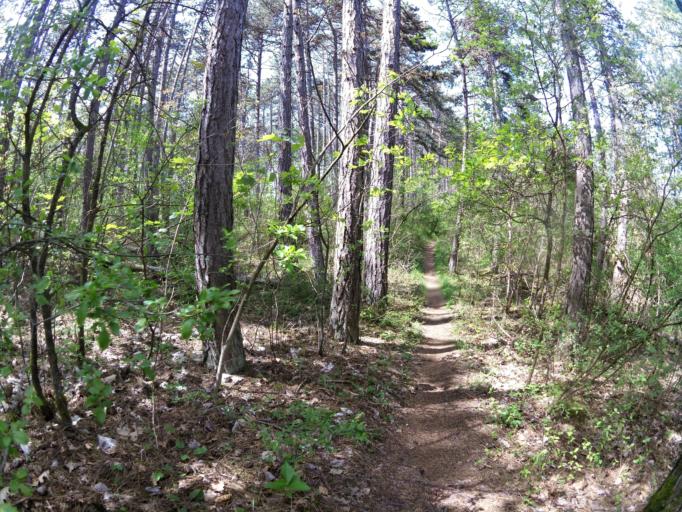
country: DE
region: Bavaria
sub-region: Regierungsbezirk Unterfranken
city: Erlabrunn
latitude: 49.8572
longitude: 9.8300
